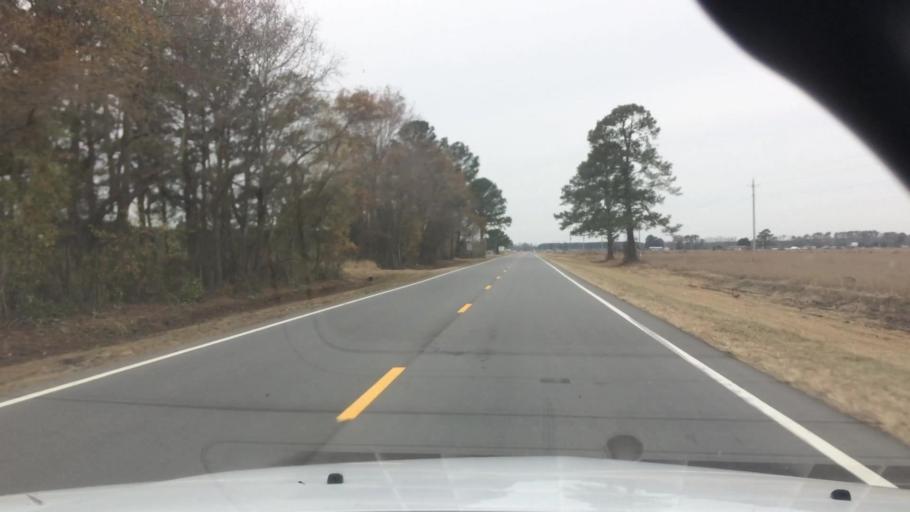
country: US
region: North Carolina
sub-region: Pitt County
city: Farmville
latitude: 35.6005
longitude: -77.6408
